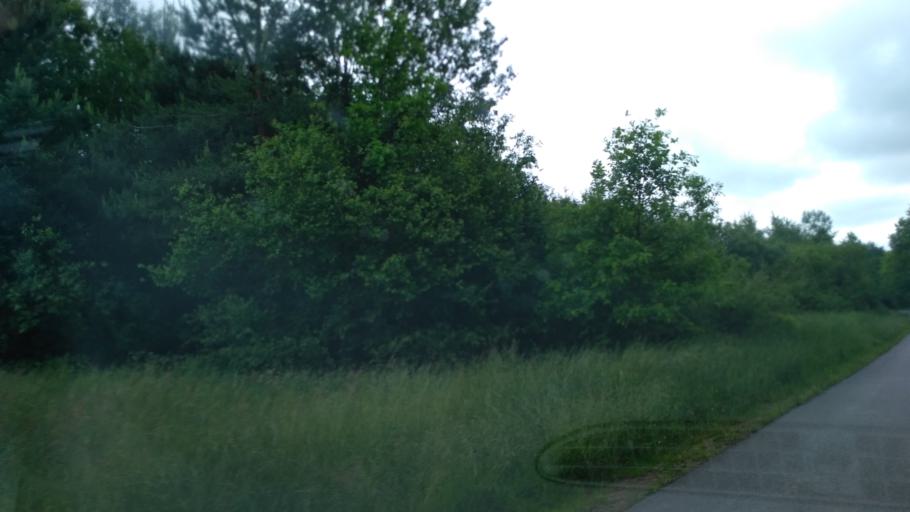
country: PL
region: Subcarpathian Voivodeship
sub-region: Powiat przemyski
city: Przedmiescie Dubieckie
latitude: 49.8755
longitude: 22.4029
